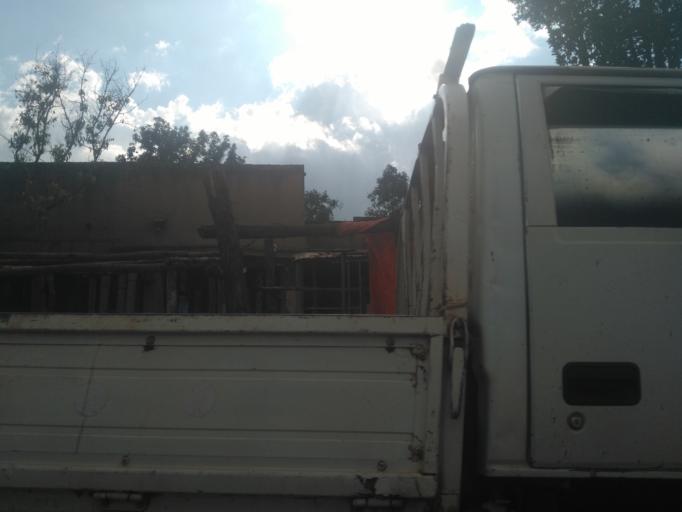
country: UG
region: Central Region
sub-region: Wakiso District
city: Kajansi
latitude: 0.2673
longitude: 32.4367
